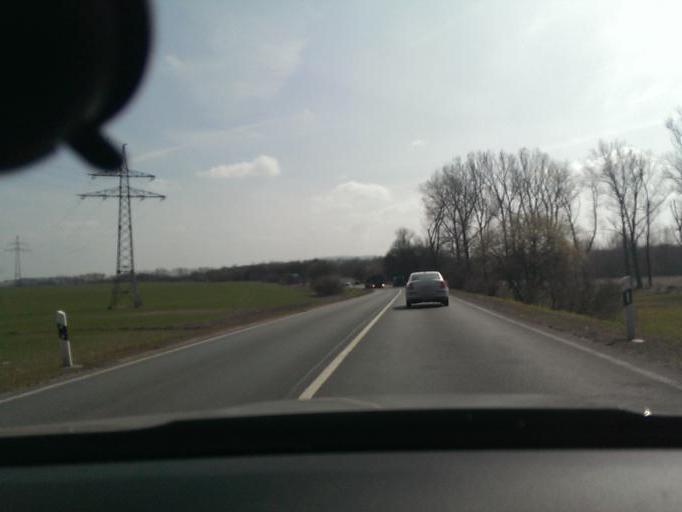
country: DE
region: Thuringia
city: Hohenkirchen
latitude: 50.8474
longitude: 10.7101
